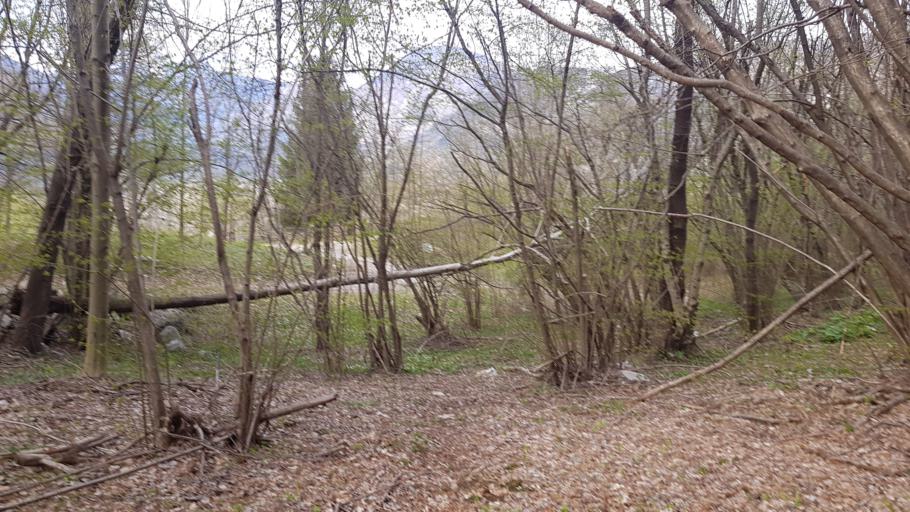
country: IT
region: Friuli Venezia Giulia
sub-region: Provincia di Udine
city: Trasaghis
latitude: 46.2838
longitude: 13.0426
